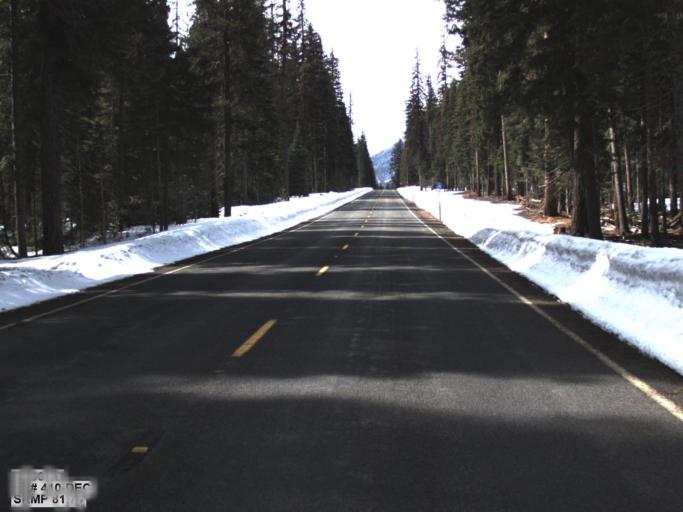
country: US
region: Washington
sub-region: Kittitas County
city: Cle Elum
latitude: 46.9540
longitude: -121.3002
